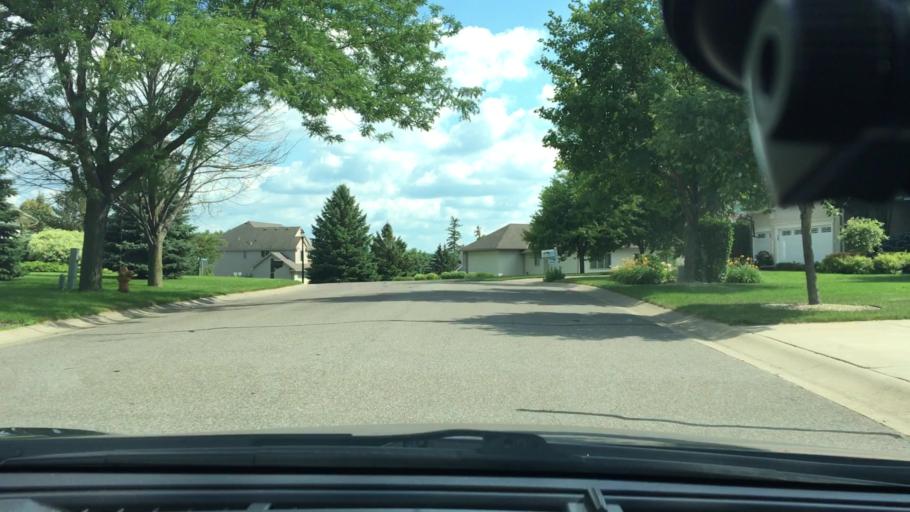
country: US
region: Minnesota
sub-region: Hennepin County
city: Plymouth
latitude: 45.0315
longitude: -93.4436
